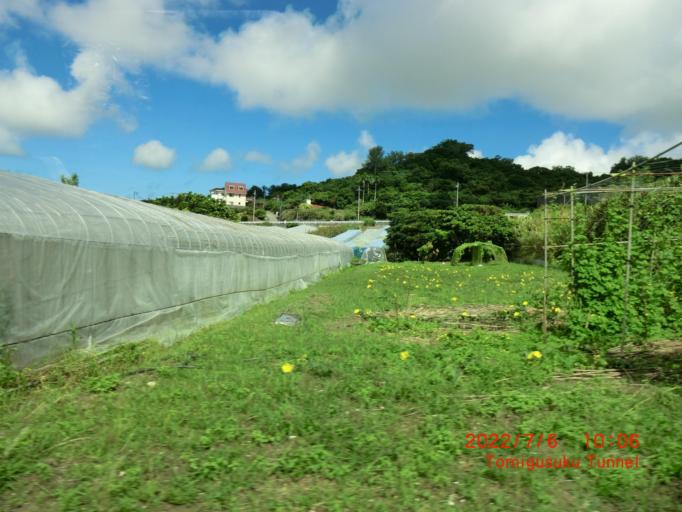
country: JP
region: Okinawa
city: Tomigusuku
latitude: 26.1703
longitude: 127.6844
